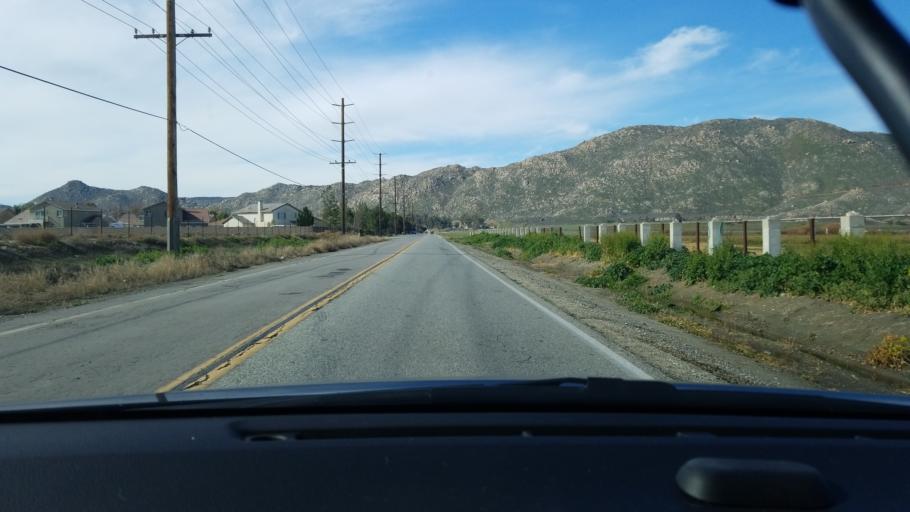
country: US
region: California
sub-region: Riverside County
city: Hemet
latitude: 33.7729
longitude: -117.0226
